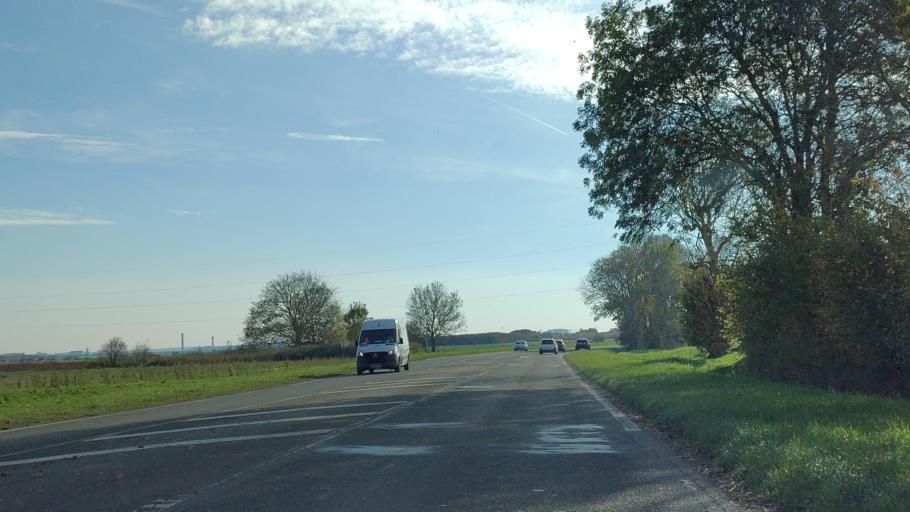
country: FR
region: Ile-de-France
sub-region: Departement du Val-d'Oise
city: Marly-la-Ville
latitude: 49.0717
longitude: 2.5286
